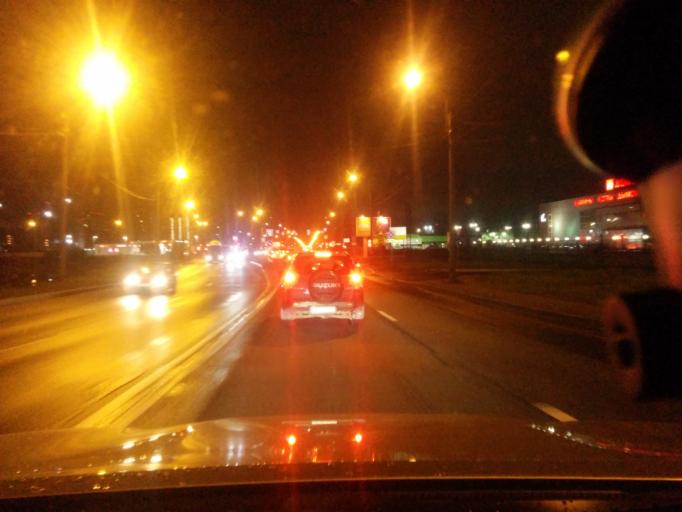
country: RU
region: Leningrad
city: Parnas
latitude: 60.0638
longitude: 30.3435
